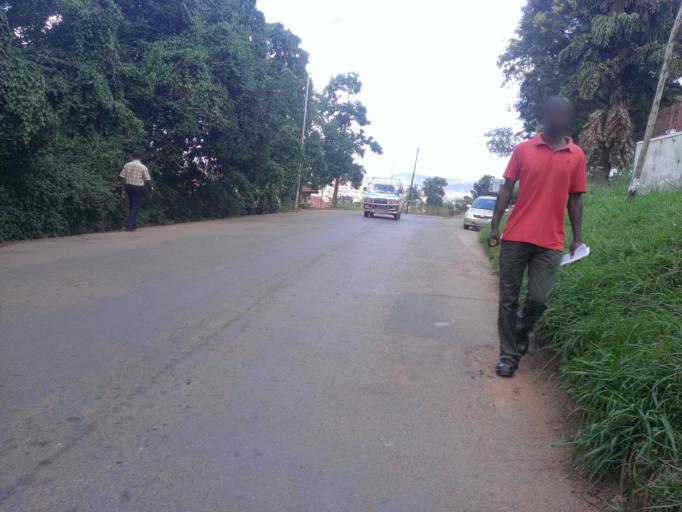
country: UG
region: Central Region
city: Kampala Central Division
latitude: 0.3158
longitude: 32.5604
